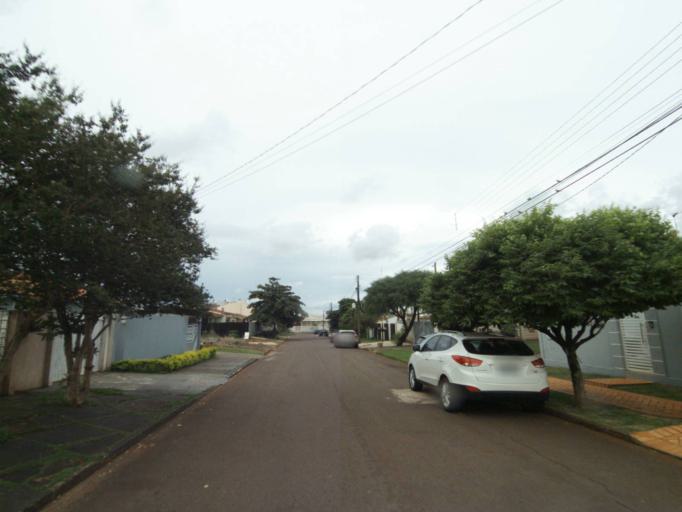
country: BR
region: Parana
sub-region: Campo Mourao
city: Campo Mourao
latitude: -24.0347
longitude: -52.3624
